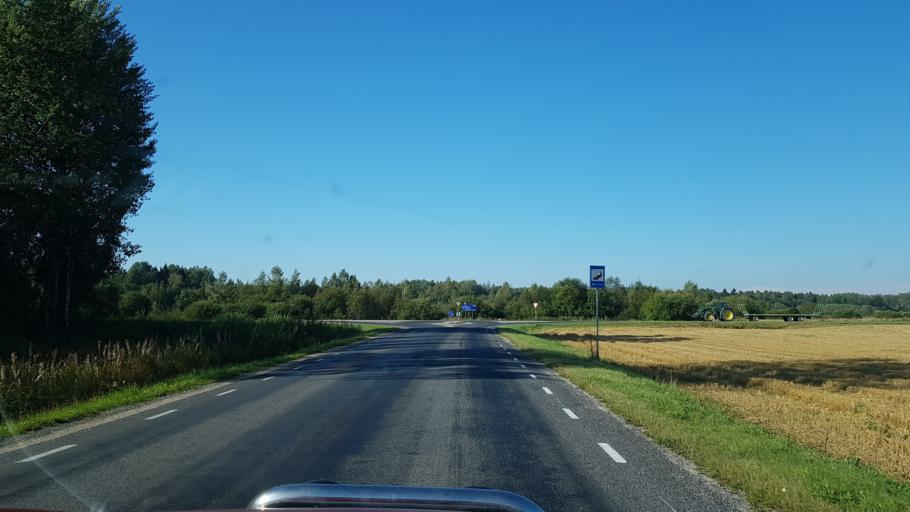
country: EE
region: Jogevamaa
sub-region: Jogeva linn
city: Jogeva
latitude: 58.6897
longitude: 26.3579
